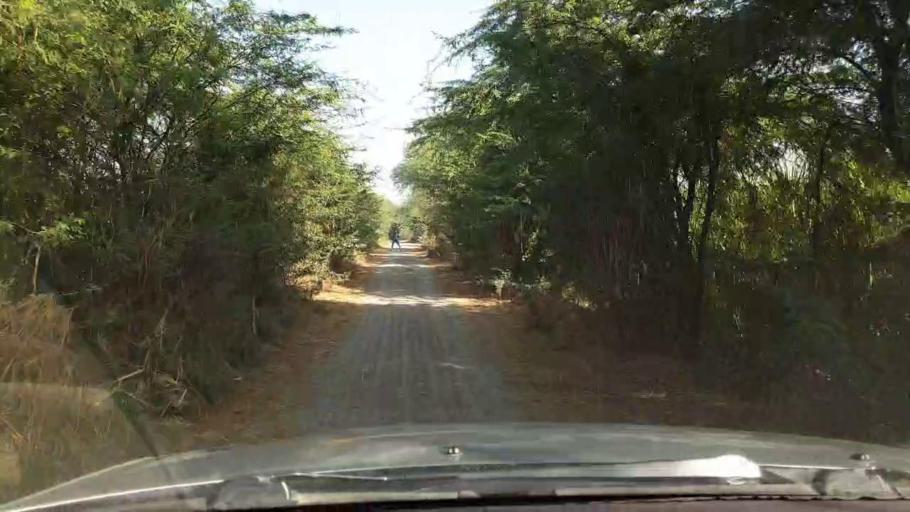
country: PK
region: Sindh
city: Matli
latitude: 25.0250
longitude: 68.5734
